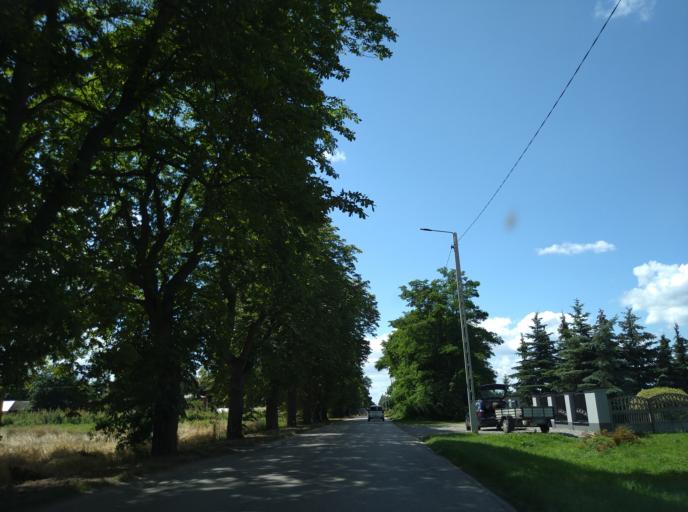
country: PL
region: Masovian Voivodeship
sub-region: Powiat bialobrzeski
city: Bialobrzegi
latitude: 51.6712
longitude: 20.9221
